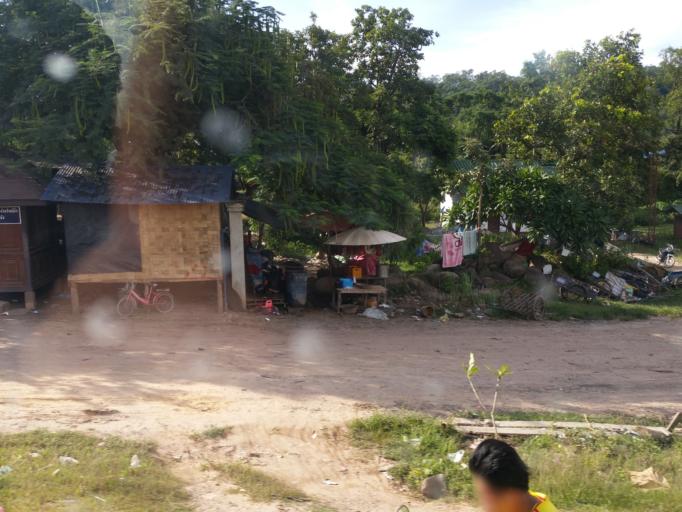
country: TH
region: Changwat Ubon Ratchathani
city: Sirindhorn
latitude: 15.1294
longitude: 105.4732
